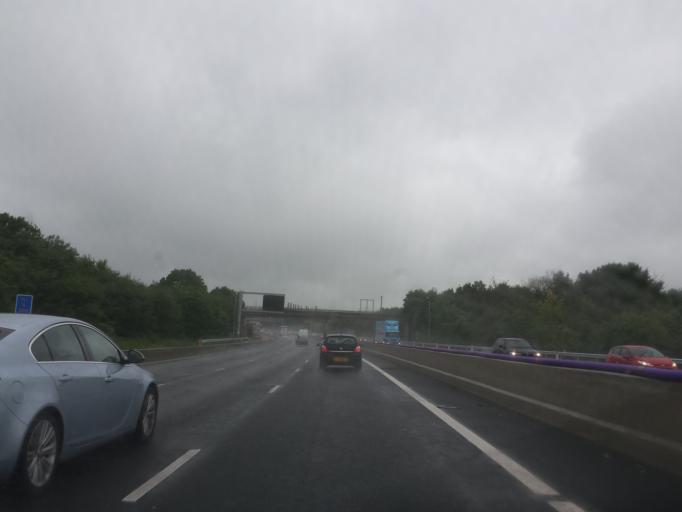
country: GB
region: England
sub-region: Derbyshire
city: Blackwell
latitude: 53.1134
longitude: -1.3330
